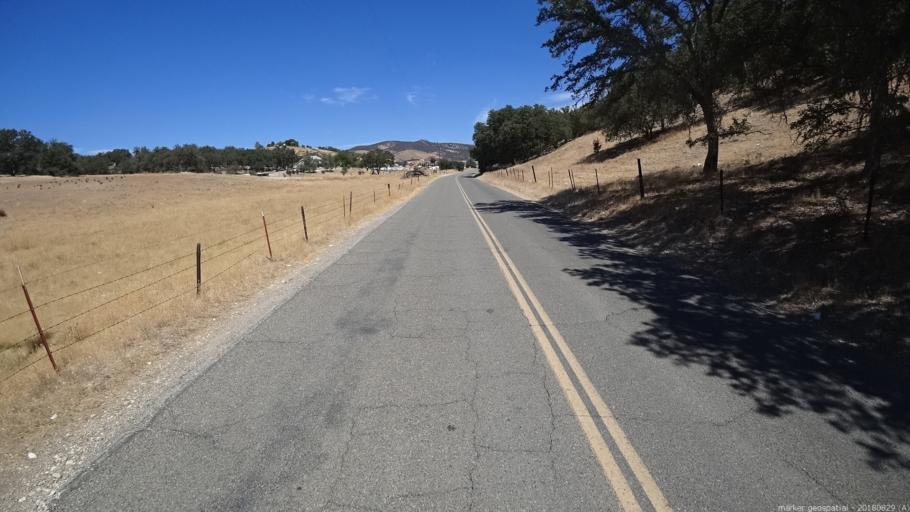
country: US
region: California
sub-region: San Luis Obispo County
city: Lake Nacimiento
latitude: 35.8924
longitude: -120.9899
